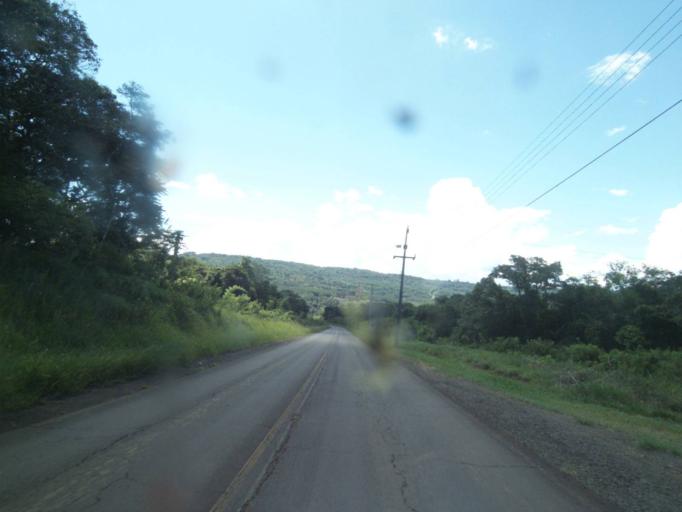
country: BR
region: Parana
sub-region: Chopinzinho
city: Chopinzinho
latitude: -25.7763
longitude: -52.1122
